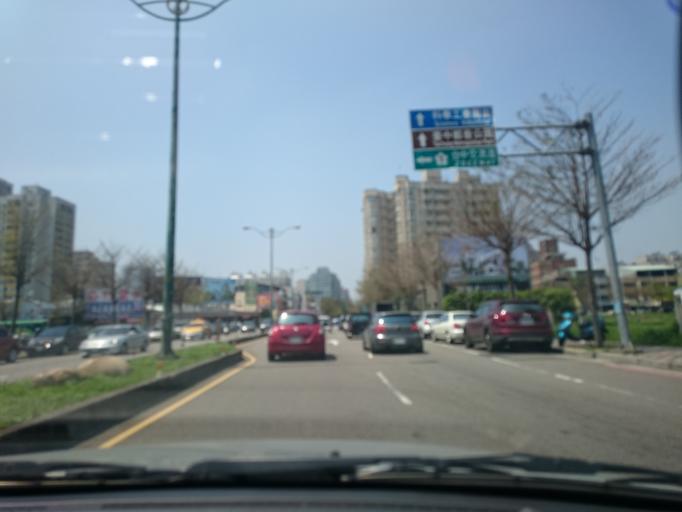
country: TW
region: Taiwan
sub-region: Taichung City
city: Taichung
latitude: 24.1818
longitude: 120.6259
